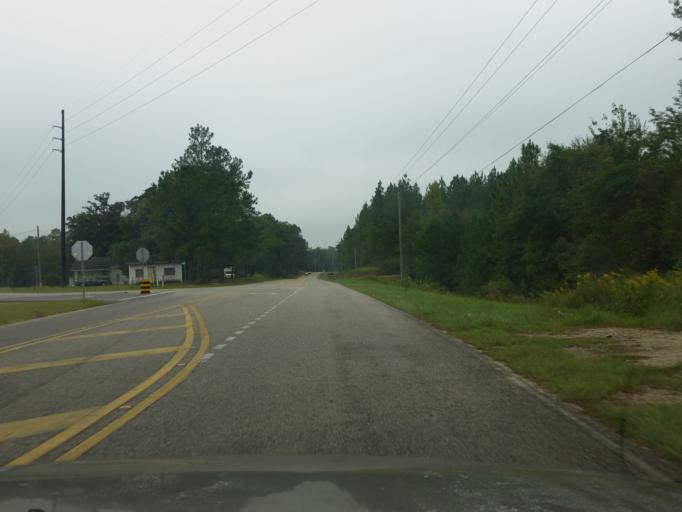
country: US
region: Alabama
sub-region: Baldwin County
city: Bay Minette
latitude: 30.8594
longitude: -87.8016
